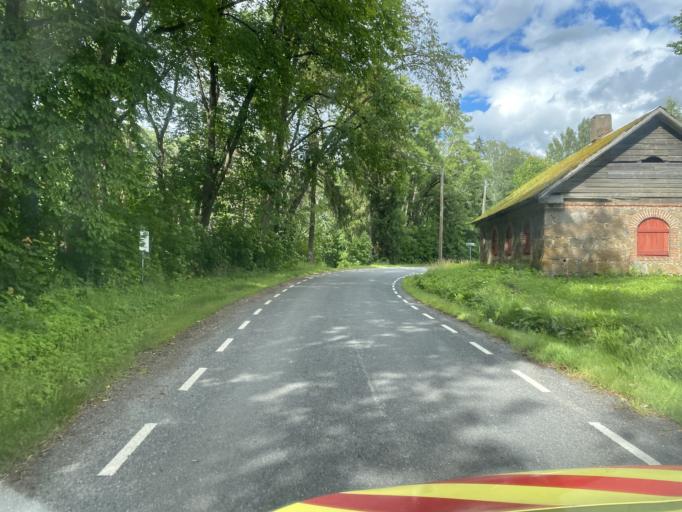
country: EE
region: Viljandimaa
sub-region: Viiratsi vald
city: Viiratsi
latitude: 58.3963
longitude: 25.7644
